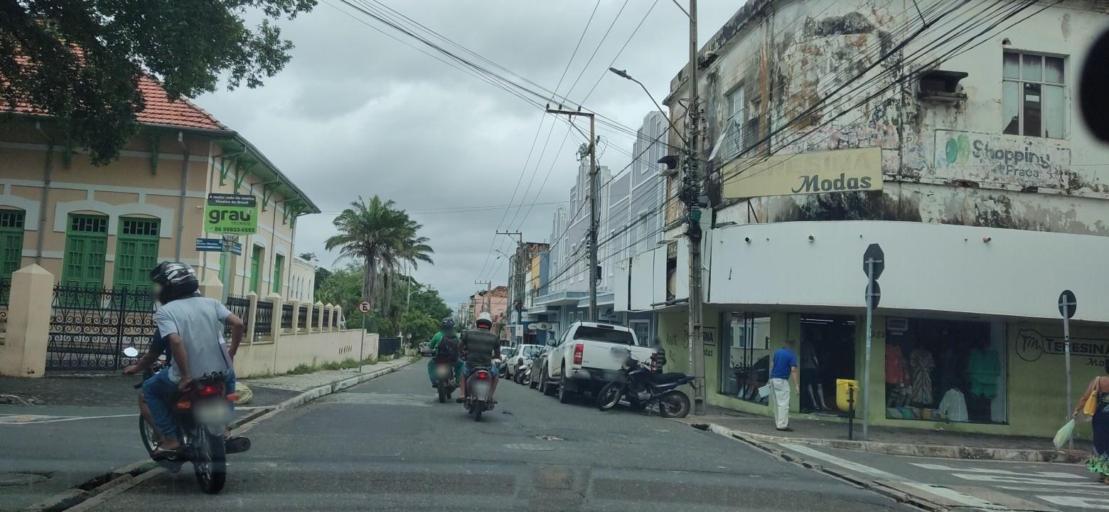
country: BR
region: Piaui
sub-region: Teresina
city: Teresina
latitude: -5.0904
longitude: -42.8142
